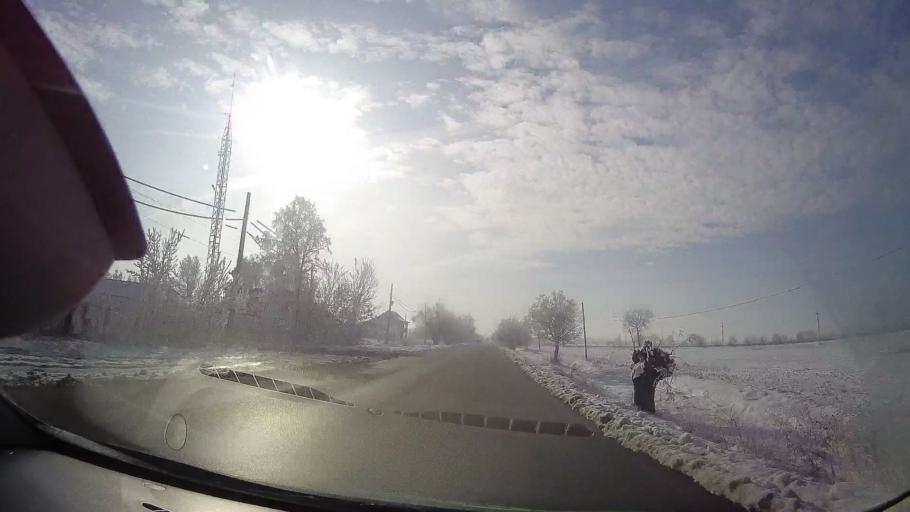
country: RO
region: Neamt
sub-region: Comuna Timisesti
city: Timisesti
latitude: 47.2430
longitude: 26.5412
